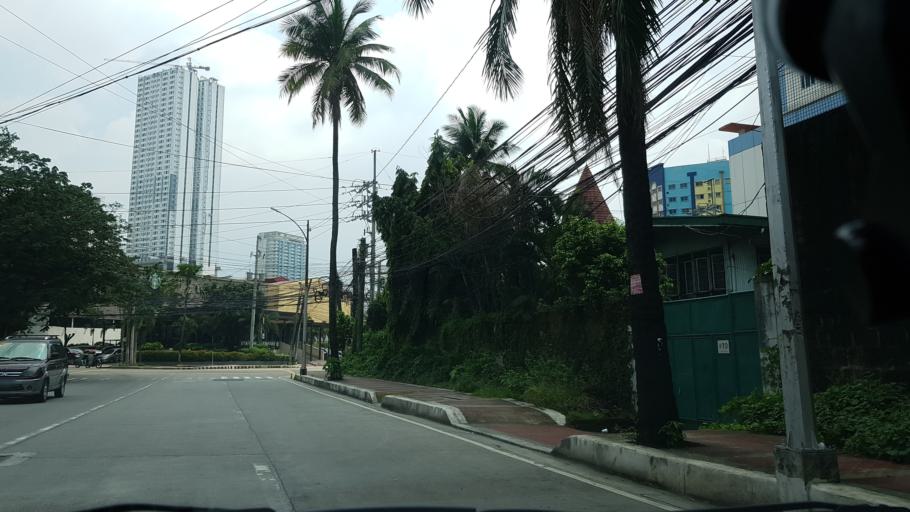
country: PH
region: Calabarzon
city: Del Monte
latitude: 14.6398
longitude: 121.0338
